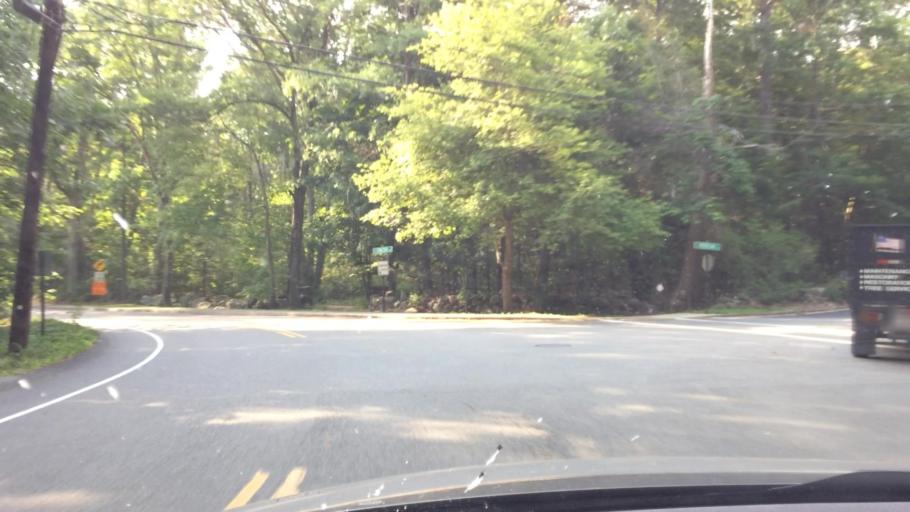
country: US
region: Massachusetts
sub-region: Middlesex County
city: Weston
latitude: 42.3774
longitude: -71.3114
